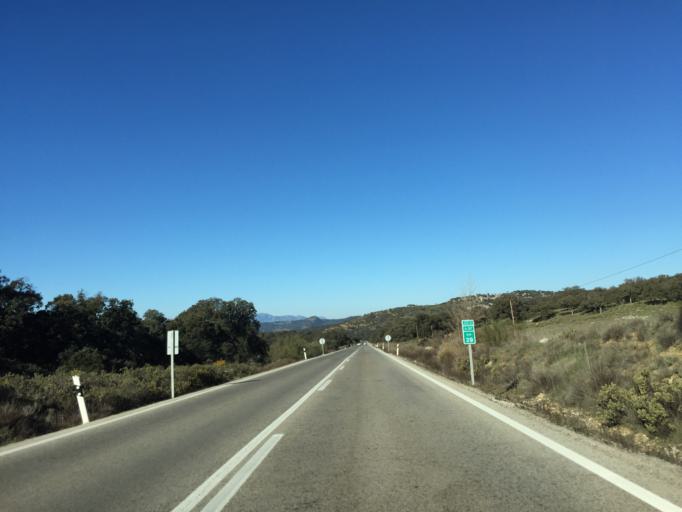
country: ES
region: Andalusia
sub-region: Provincia de Malaga
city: Cuevas del Becerro
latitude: 36.8319
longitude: -5.0730
